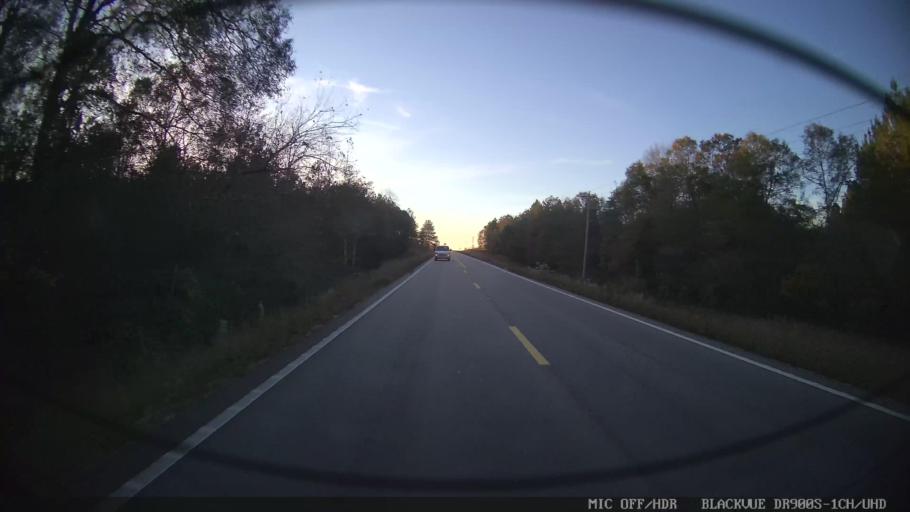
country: US
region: Mississippi
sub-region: Lamar County
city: Lumberton
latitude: 30.9912
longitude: -89.2746
